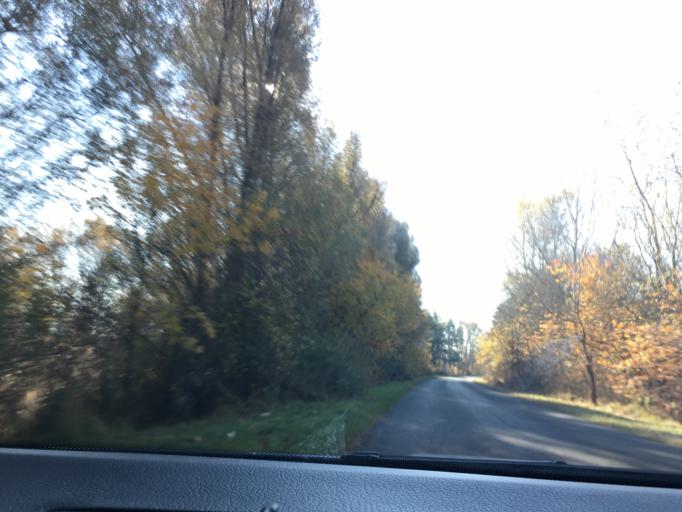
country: HU
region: Hajdu-Bihar
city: Hajdusamson
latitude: 47.5064
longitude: 21.7386
